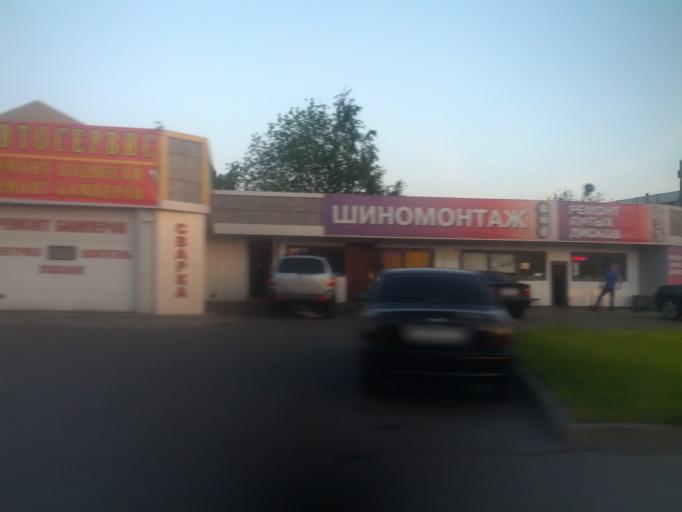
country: RU
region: St.-Petersburg
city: Staraya Derevnya
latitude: 59.9953
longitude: 30.2542
